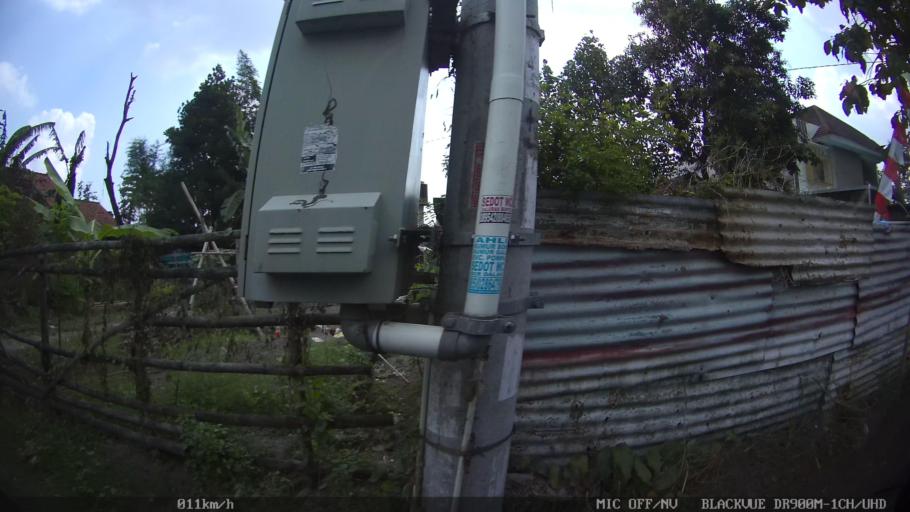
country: ID
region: Daerah Istimewa Yogyakarta
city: Yogyakarta
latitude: -7.8185
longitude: 110.4058
